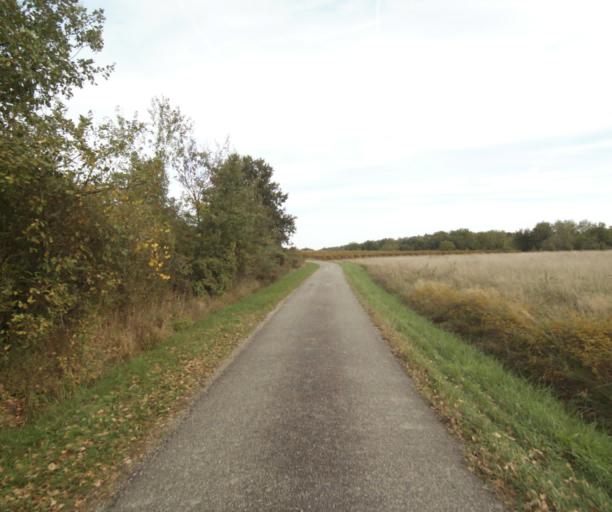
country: FR
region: Midi-Pyrenees
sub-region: Departement du Tarn-et-Garonne
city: Orgueil
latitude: 43.8821
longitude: 1.3906
